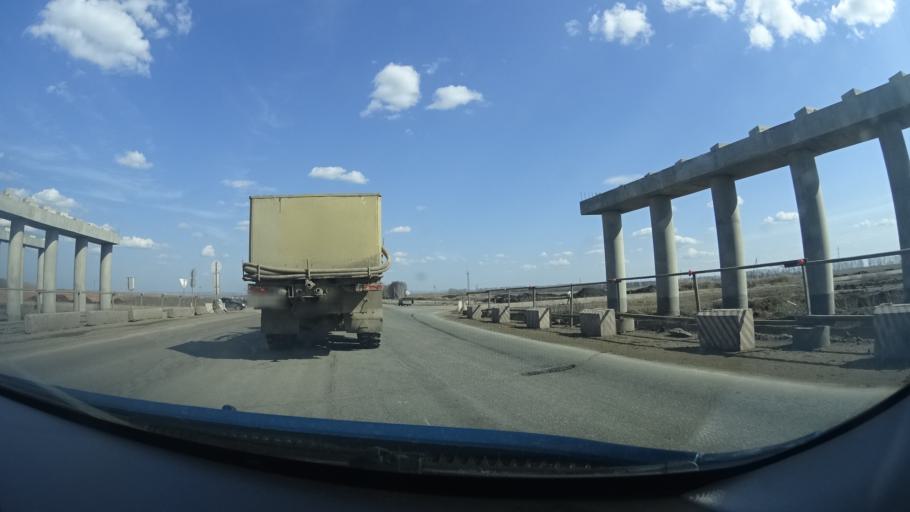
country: RU
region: Bashkortostan
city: Buzdyak
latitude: 54.6435
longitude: 54.5363
